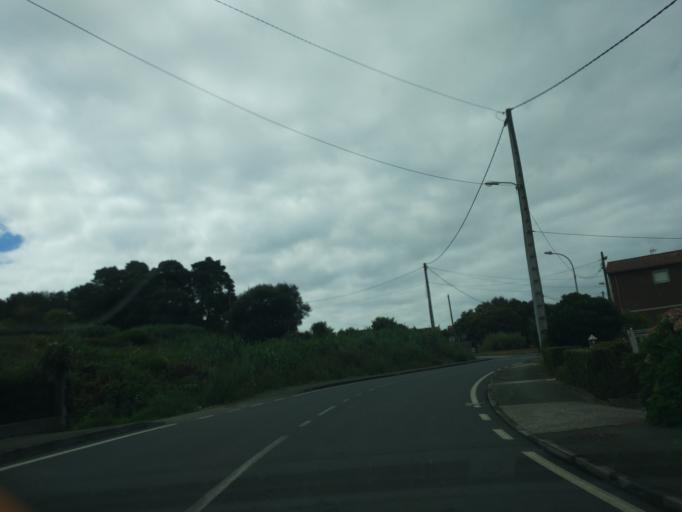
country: ES
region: Galicia
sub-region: Provincia da Coruna
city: Boiro
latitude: 42.6420
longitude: -8.8594
